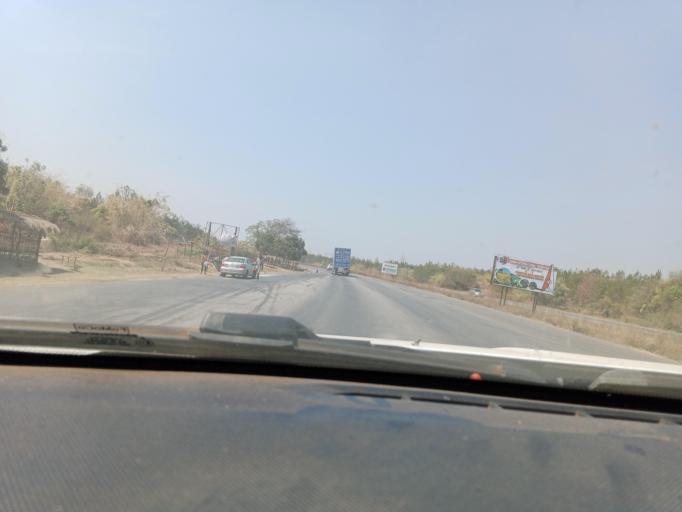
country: ZM
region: Copperbelt
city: Luanshya
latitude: -13.0420
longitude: 28.4617
